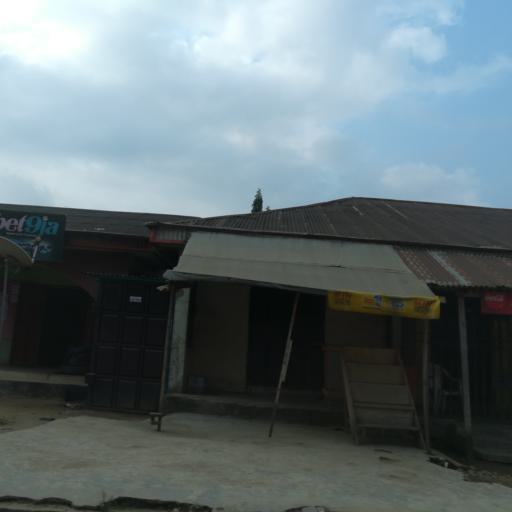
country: NG
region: Rivers
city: Okrika
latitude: 4.7836
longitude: 7.1393
